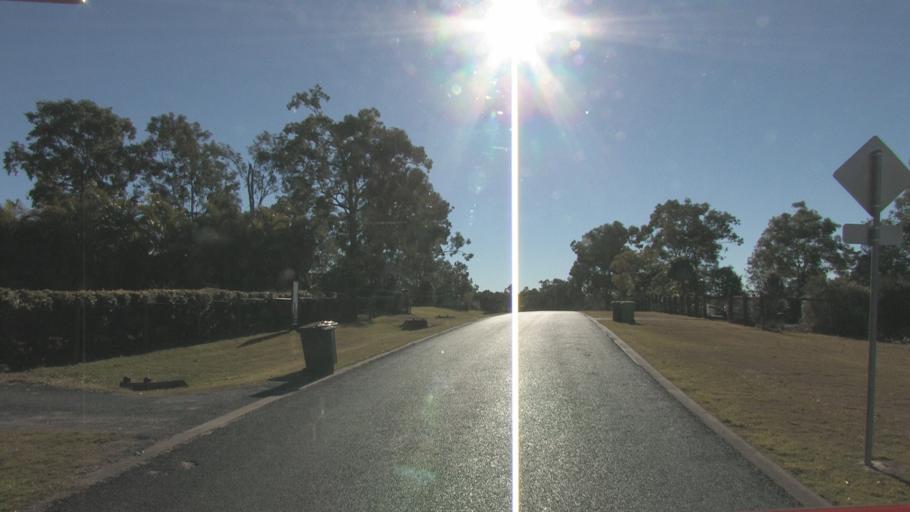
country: AU
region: Queensland
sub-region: Logan
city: North Maclean
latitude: -27.7438
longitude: 152.9628
